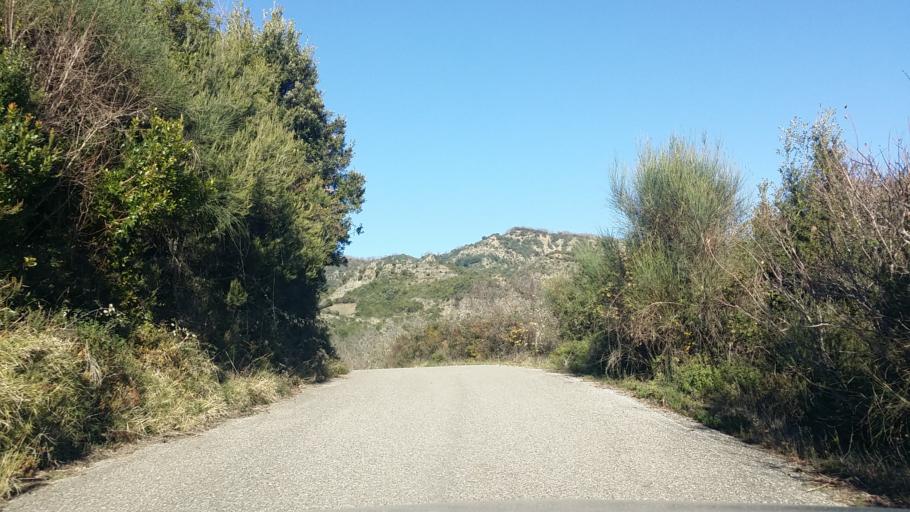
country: GR
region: West Greece
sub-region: Nomos Aitolias kai Akarnanias
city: Krikellos
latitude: 39.0047
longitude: 21.2413
